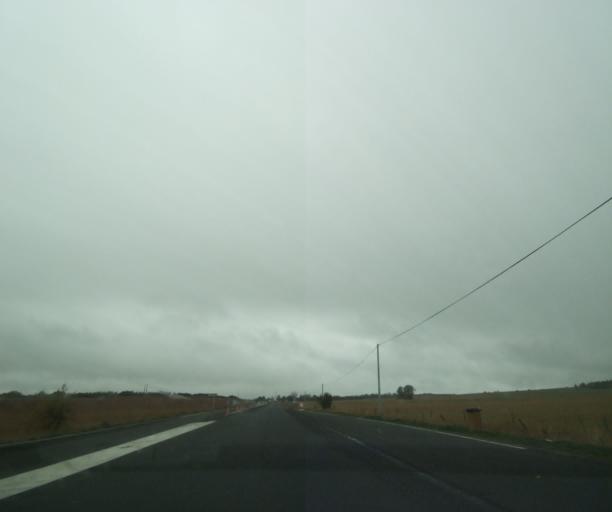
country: FR
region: Midi-Pyrenees
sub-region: Departement de l'Aveyron
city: Millau
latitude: 44.0799
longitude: 3.1212
